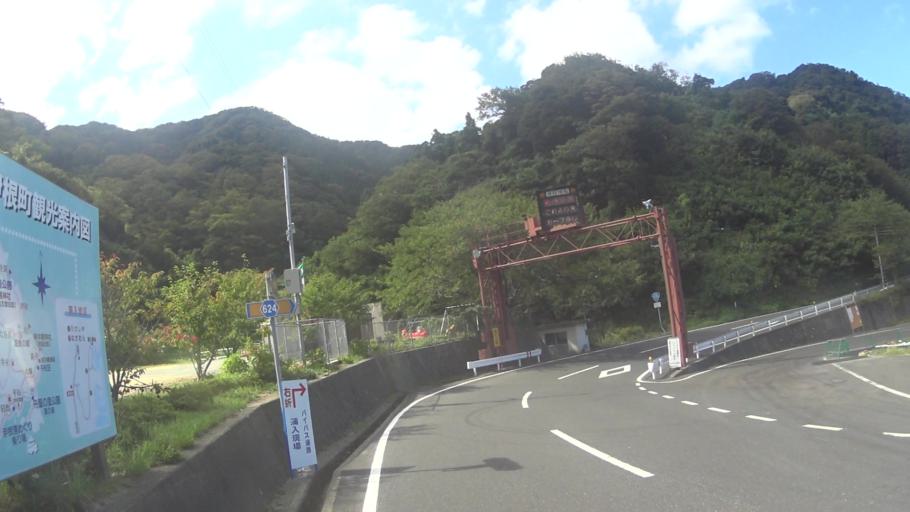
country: JP
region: Kyoto
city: Miyazu
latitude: 35.7511
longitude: 135.2500
